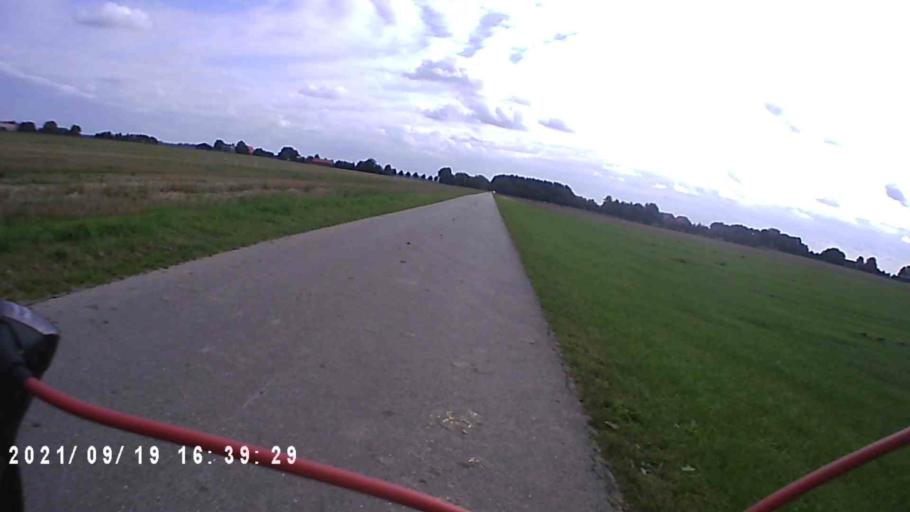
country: NL
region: Groningen
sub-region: Gemeente  Oldambt
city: Winschoten
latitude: 53.1889
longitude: 7.1319
